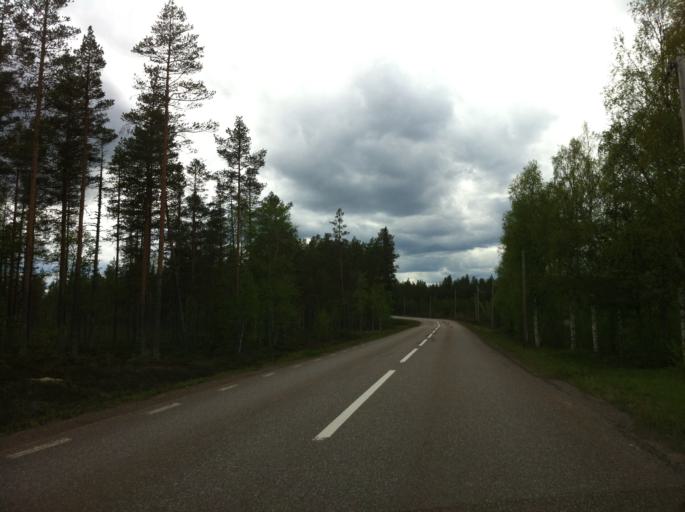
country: NO
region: Hedmark
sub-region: Trysil
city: Innbygda
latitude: 61.4308
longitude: 13.0941
